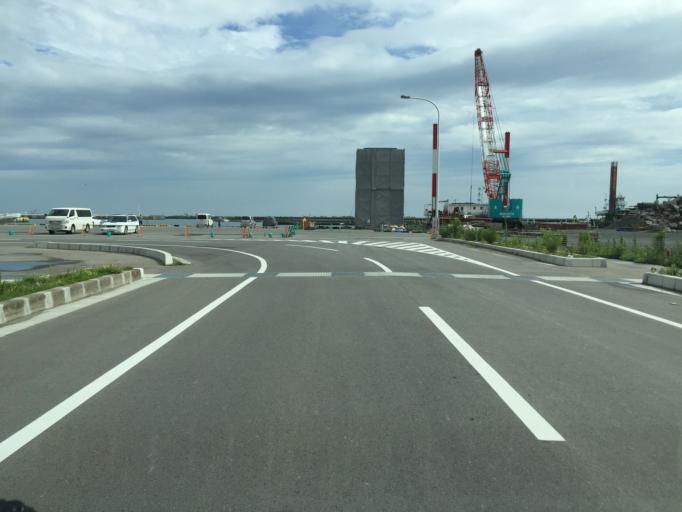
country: JP
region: Miyagi
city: Marumori
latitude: 37.8272
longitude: 140.9740
